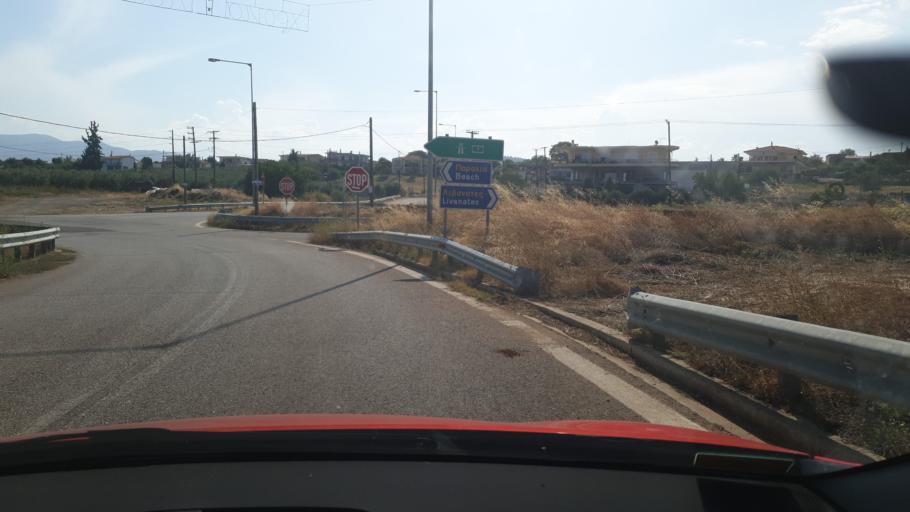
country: GR
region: Central Greece
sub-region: Nomos Fthiotidos
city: Livanates
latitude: 38.7070
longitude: 23.0549
